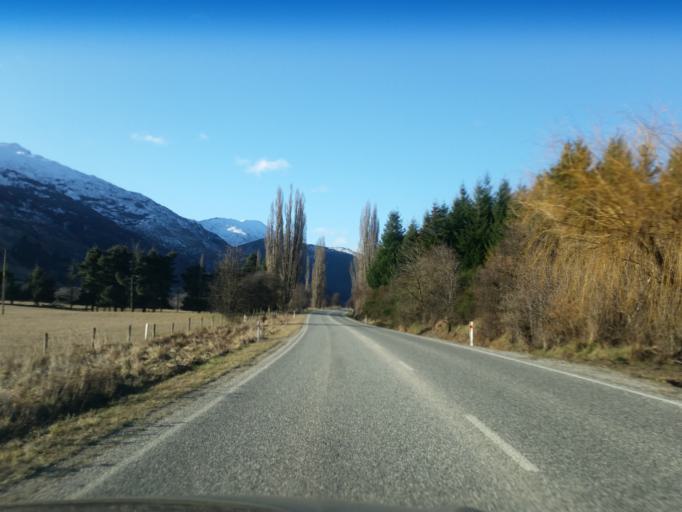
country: NZ
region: Otago
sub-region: Queenstown-Lakes District
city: Arrowtown
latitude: -44.9606
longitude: 168.7242
